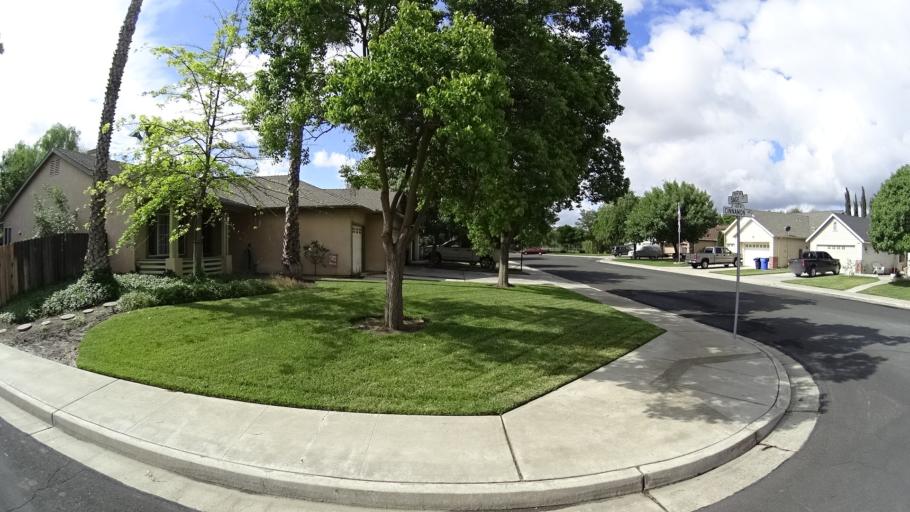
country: US
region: California
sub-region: Kings County
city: Lucerne
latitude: 36.3657
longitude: -119.6521
